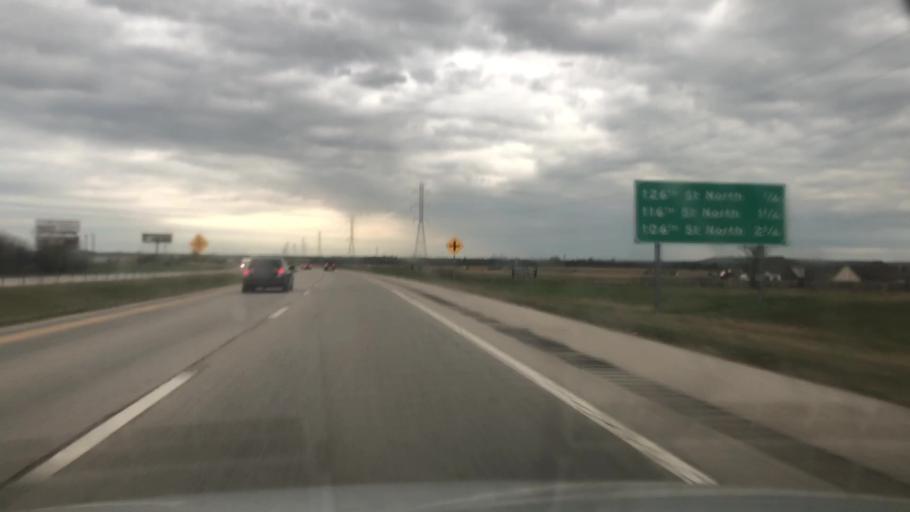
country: US
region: Oklahoma
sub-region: Tulsa County
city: Sperry
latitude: 36.3403
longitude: -95.9240
